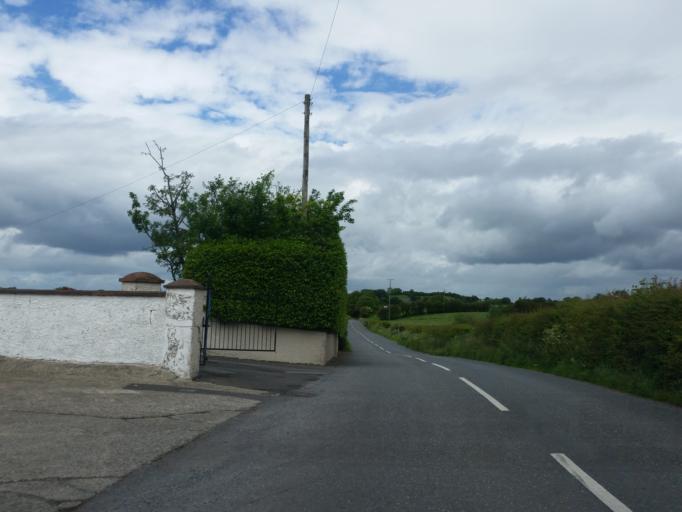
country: GB
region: Northern Ireland
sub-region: Omagh District
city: Omagh
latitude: 54.5473
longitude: -7.1166
